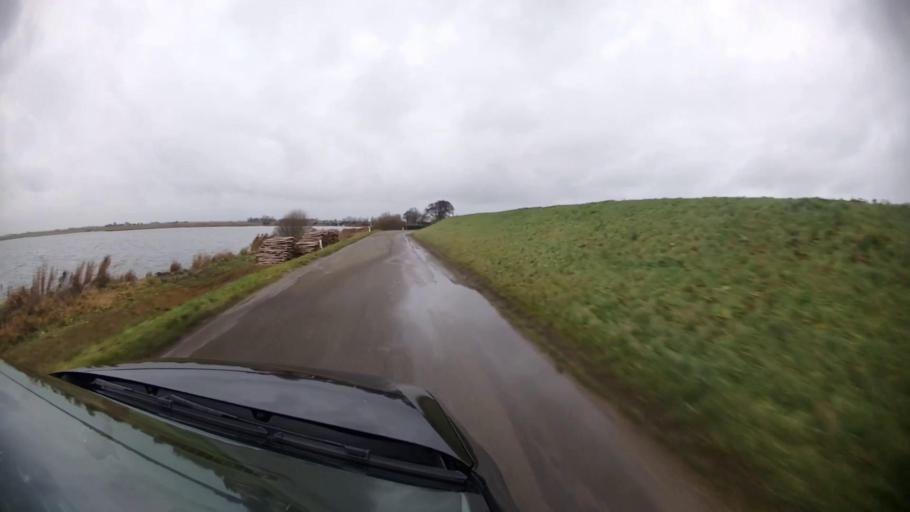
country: NL
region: North Holland
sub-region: Gemeente Waterland
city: Broek in Waterland
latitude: 52.3949
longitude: 5.0275
